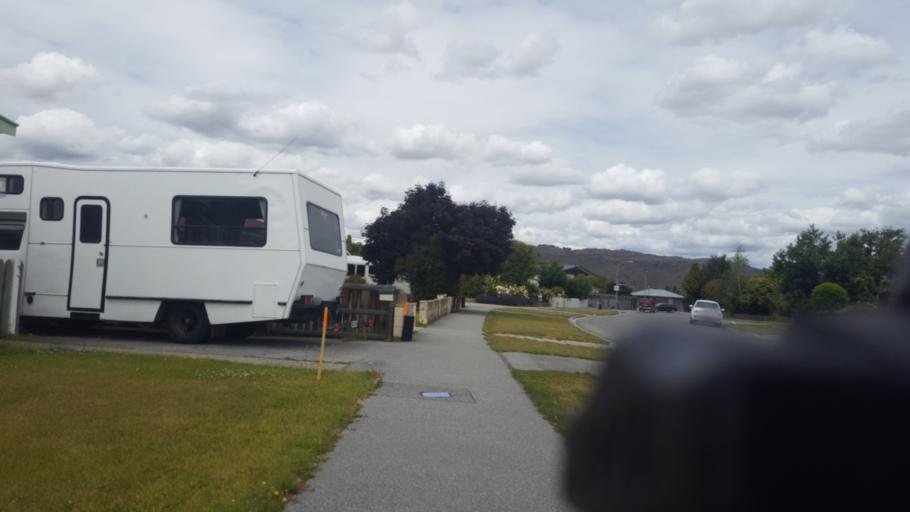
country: NZ
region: Otago
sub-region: Queenstown-Lakes District
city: Wanaka
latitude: -45.2457
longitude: 169.3806
